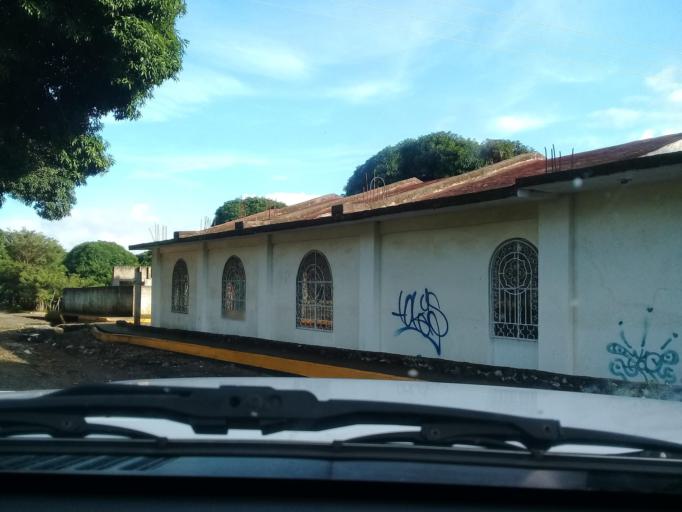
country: MX
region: Veracruz
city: Catemaco
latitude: 18.4302
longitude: -95.1113
